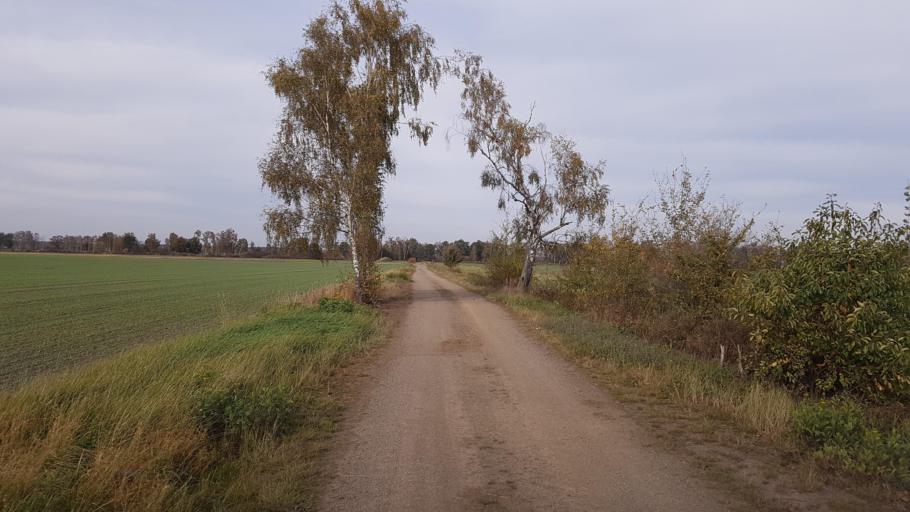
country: DE
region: Brandenburg
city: Schraden
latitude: 51.4541
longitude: 13.6913
